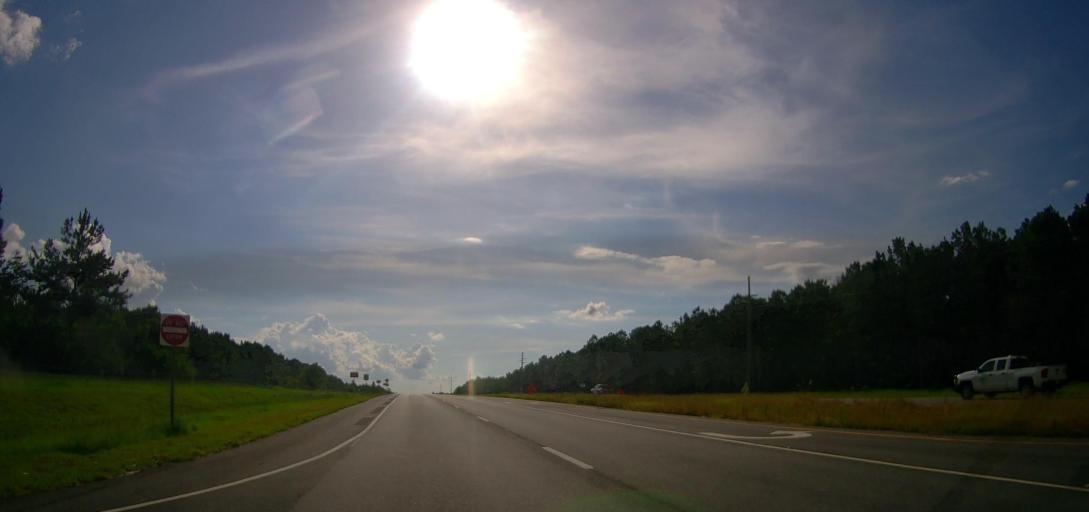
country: US
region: Georgia
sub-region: Talbot County
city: Talbotton
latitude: 32.5943
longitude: -84.4066
